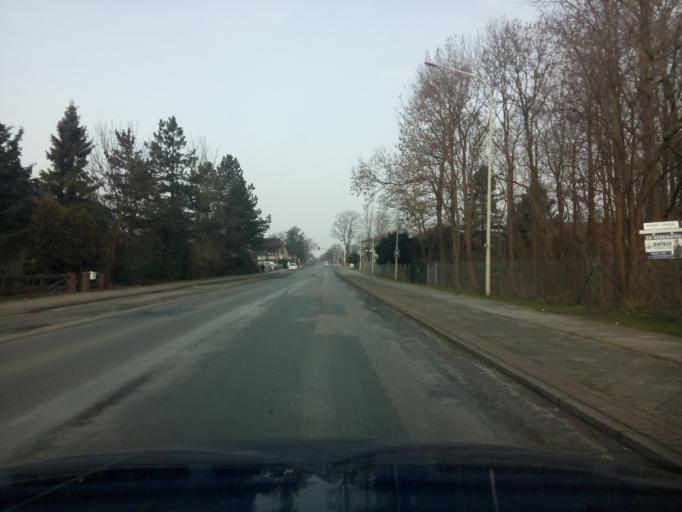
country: DE
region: Lower Saxony
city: Langen
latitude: 53.6125
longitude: 8.5966
